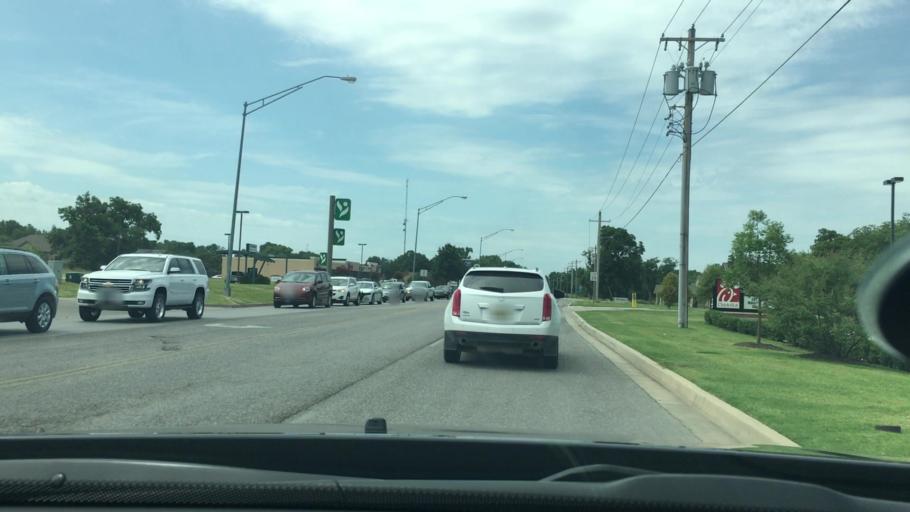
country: US
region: Oklahoma
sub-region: Carter County
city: Ardmore
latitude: 34.1872
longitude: -97.1607
